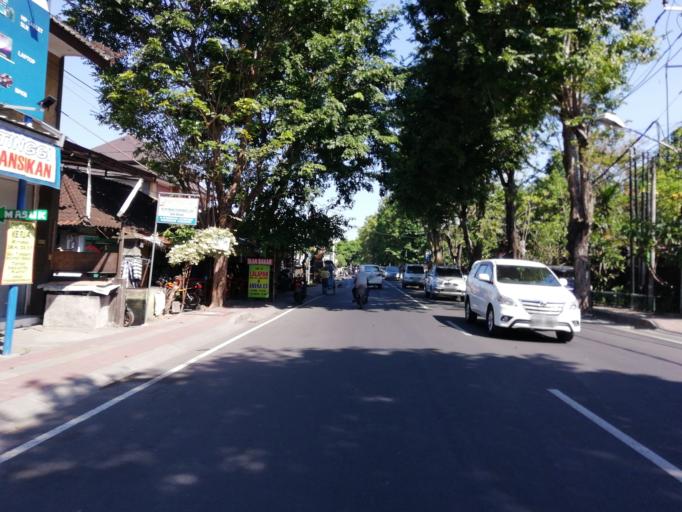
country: ID
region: Bali
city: Karyadharma
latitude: -8.7037
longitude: 115.2198
